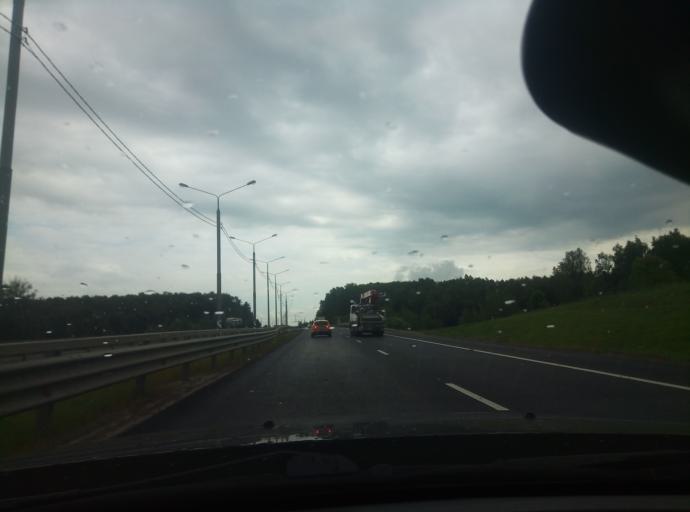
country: RU
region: Tula
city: Zaokskiy
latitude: 54.7461
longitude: 37.4931
